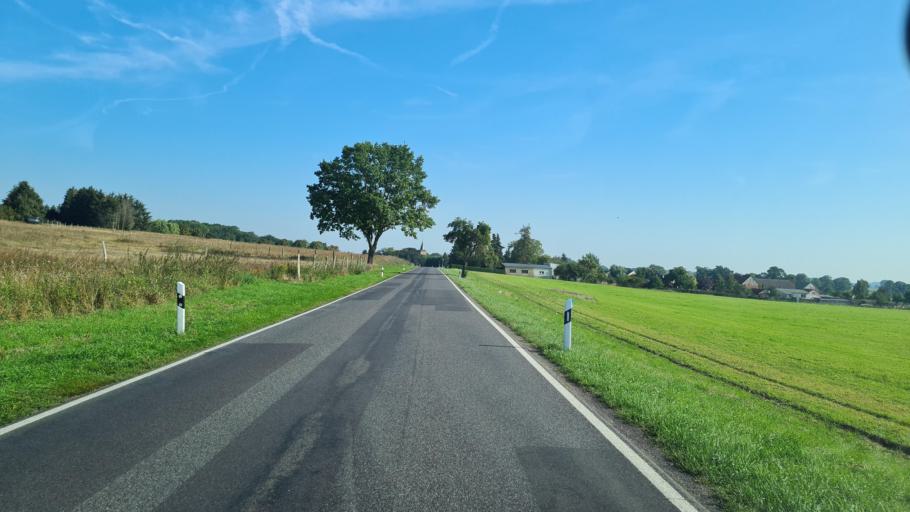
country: DE
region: Brandenburg
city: Pessin
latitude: 52.6854
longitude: 12.6467
